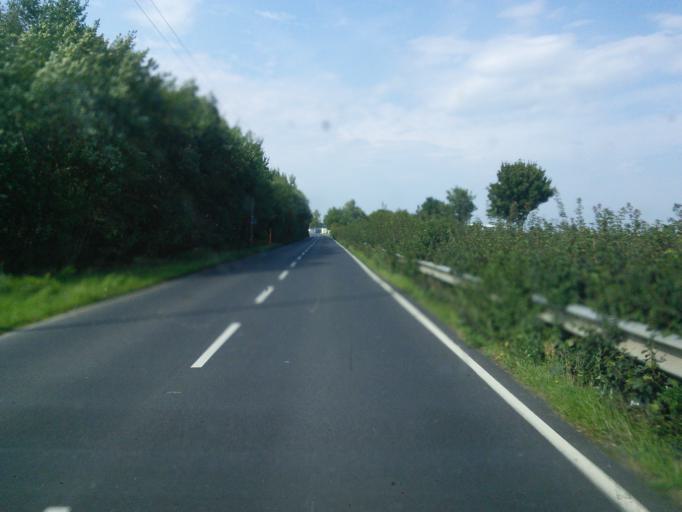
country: DE
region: North Rhine-Westphalia
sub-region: Regierungsbezirk Koln
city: Pulheim
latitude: 50.9631
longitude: 6.8194
